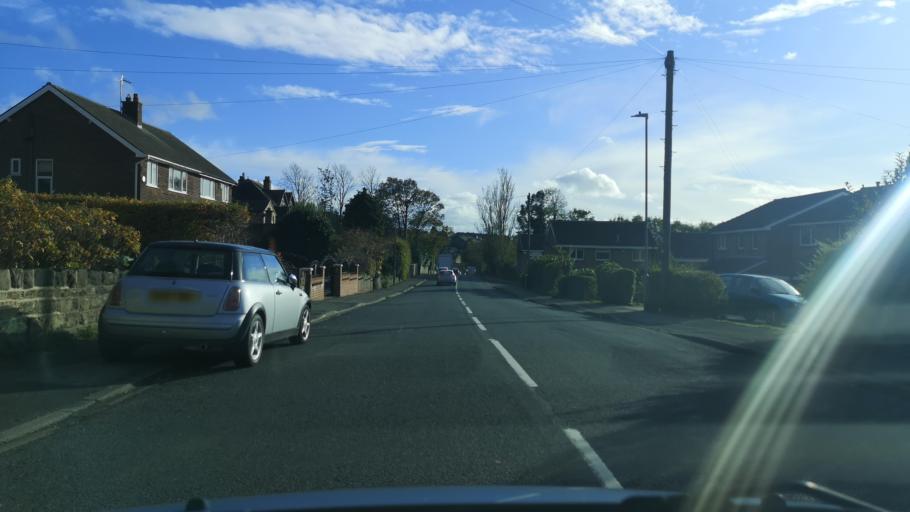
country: GB
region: England
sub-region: Kirklees
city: Heckmondwike
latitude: 53.7132
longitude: -1.6604
